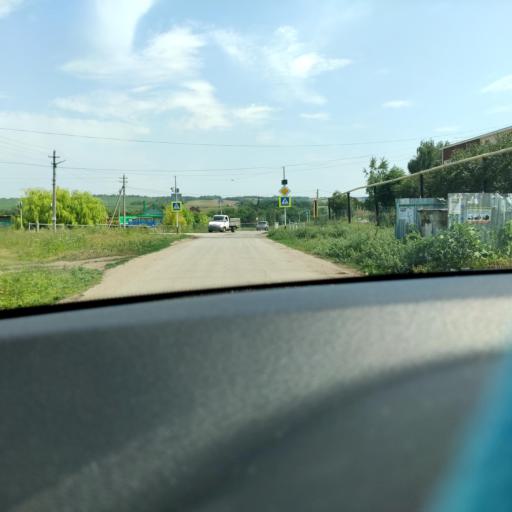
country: RU
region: Samara
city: Kinel'
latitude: 53.3413
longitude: 50.5221
